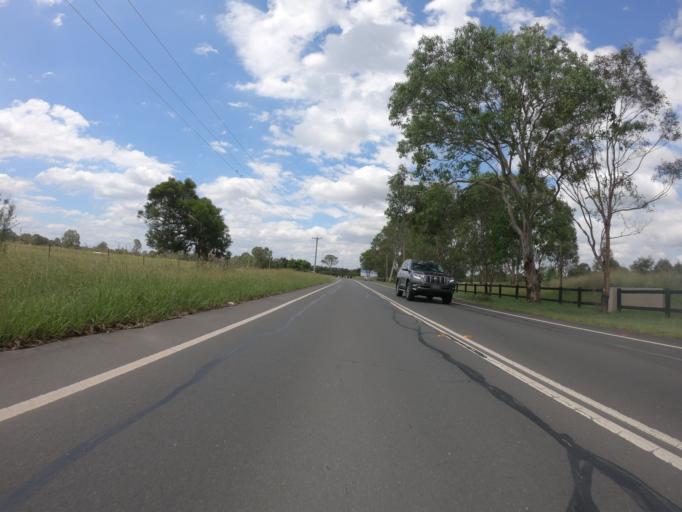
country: AU
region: New South Wales
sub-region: Penrith Municipality
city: Kingswood Park
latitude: -33.8339
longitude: 150.7558
